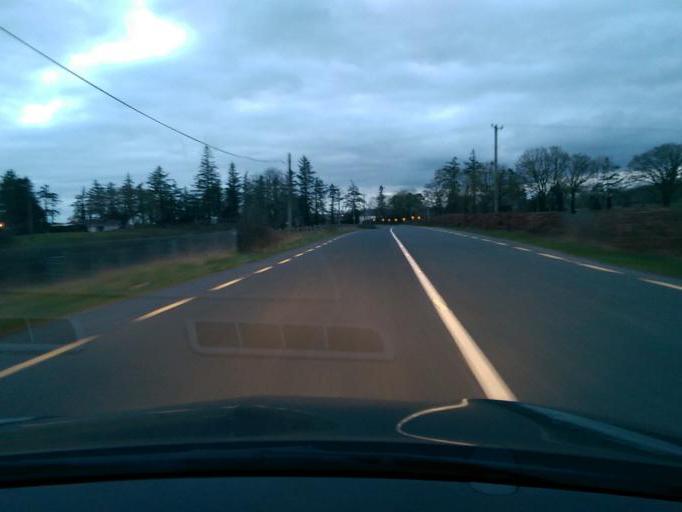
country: IE
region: Connaught
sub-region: County Galway
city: Portumna
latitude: 53.1717
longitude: -8.3224
